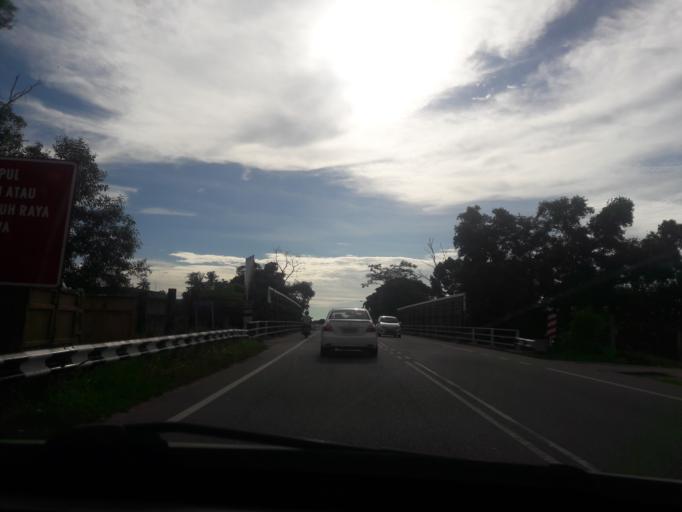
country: MY
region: Kedah
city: Sungai Petani
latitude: 5.6355
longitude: 100.5115
